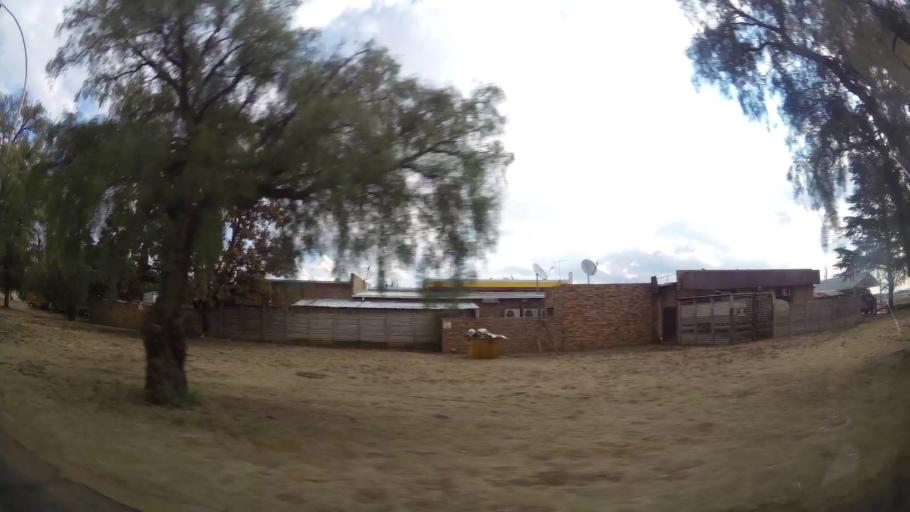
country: ZA
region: Orange Free State
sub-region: Fezile Dabi District Municipality
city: Sasolburg
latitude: -26.7983
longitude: 27.8087
